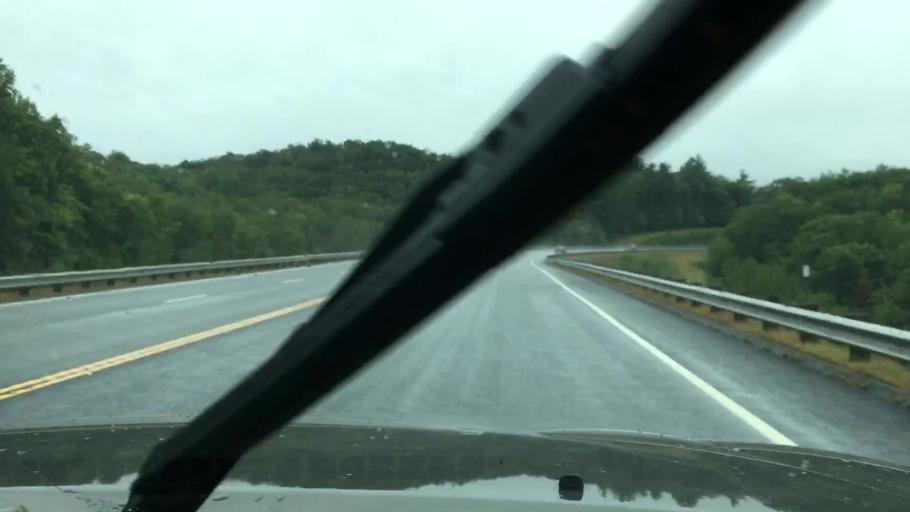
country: US
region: New Hampshire
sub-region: Cheshire County
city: Harrisville
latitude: 43.0105
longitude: -72.1422
